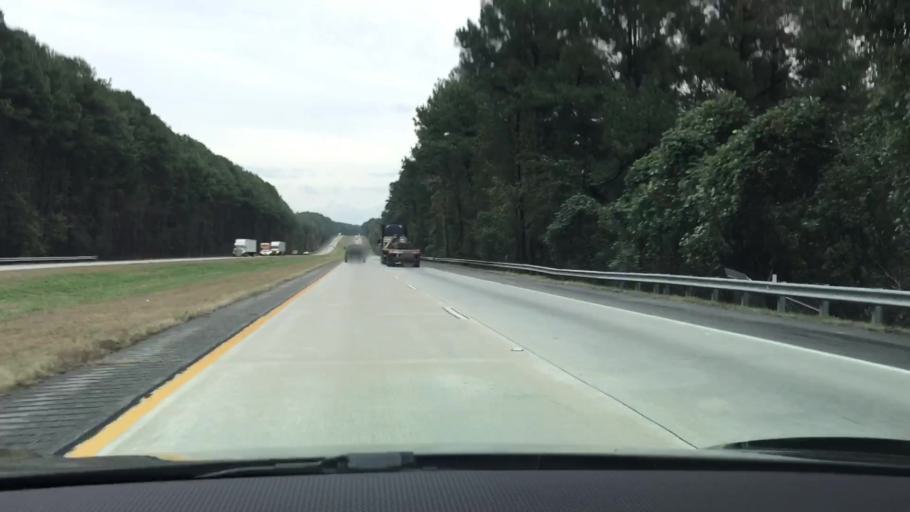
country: US
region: Georgia
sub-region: Greene County
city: Greensboro
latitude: 33.5484
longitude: -83.1536
